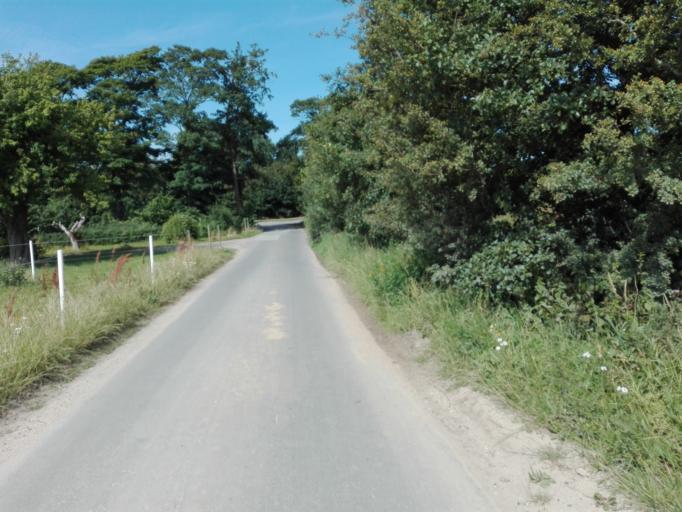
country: DK
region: Central Jutland
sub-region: Arhus Kommune
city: Marslet
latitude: 56.0838
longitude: 10.1505
